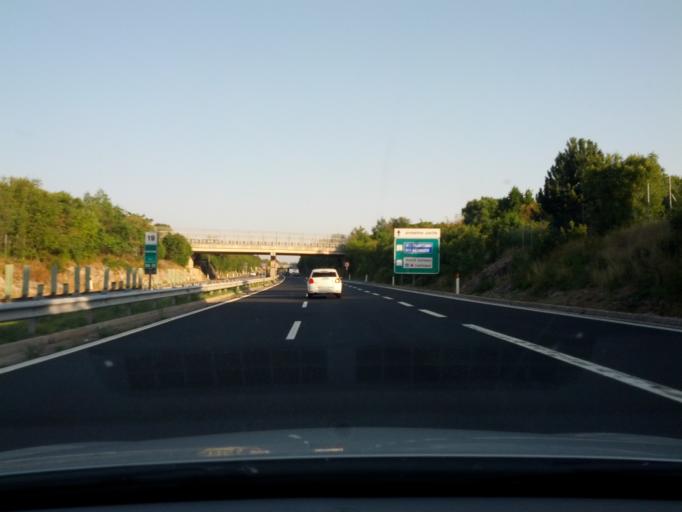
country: IT
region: Friuli Venezia Giulia
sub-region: Provincia di Trieste
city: Villa Opicina
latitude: 45.6732
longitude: 13.8201
